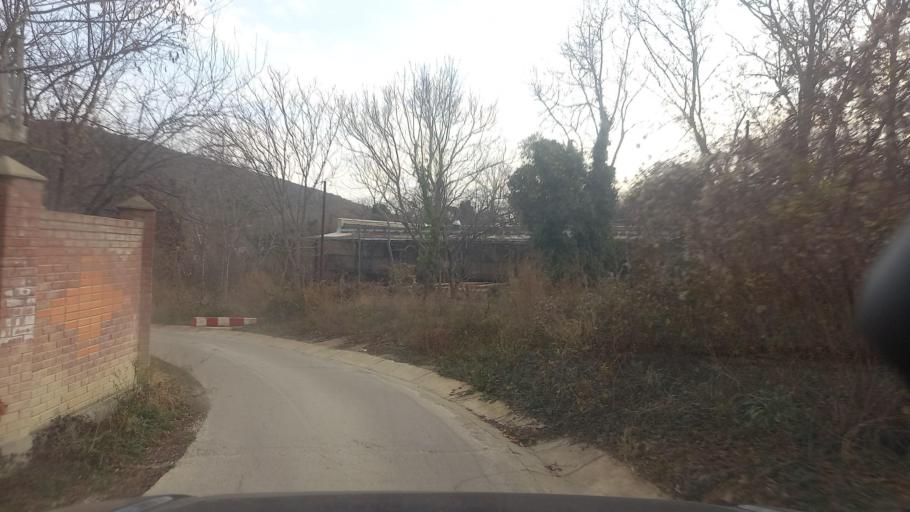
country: RU
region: Krasnodarskiy
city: Myskhako
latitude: 44.6661
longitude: 37.6823
